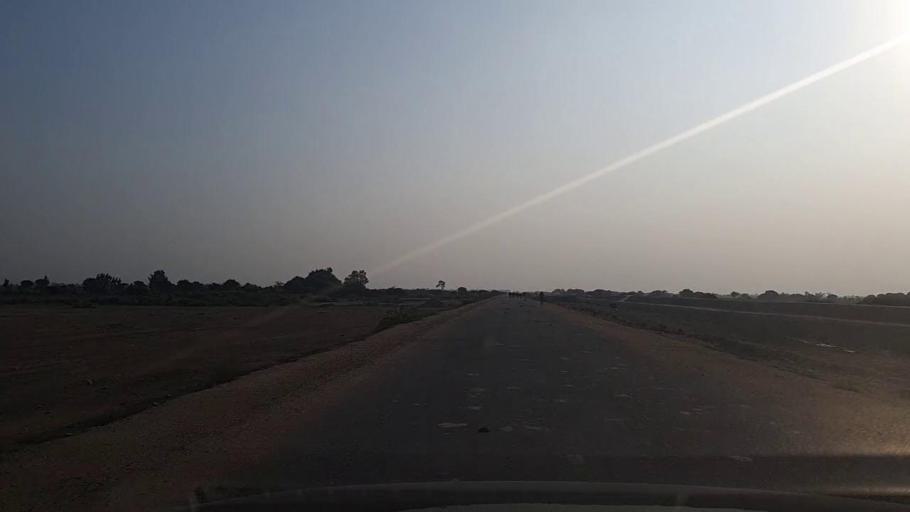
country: PK
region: Sindh
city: Mirpur Sakro
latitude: 24.4864
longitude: 67.8075
